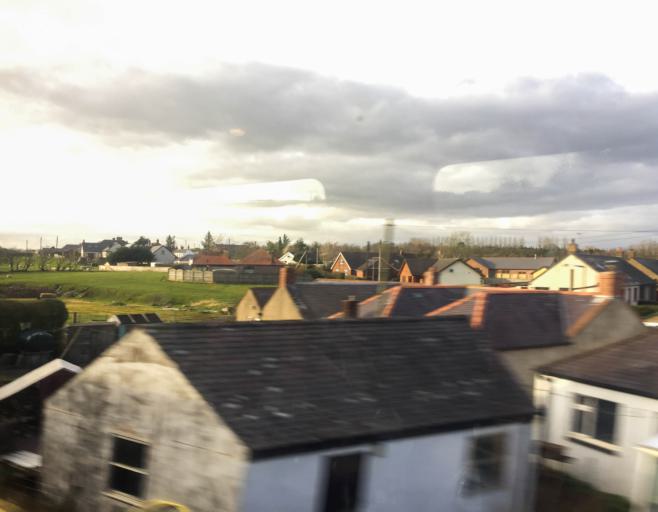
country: GB
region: Scotland
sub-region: Dumfries and Galloway
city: Annan
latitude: 55.0435
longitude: -3.1951
